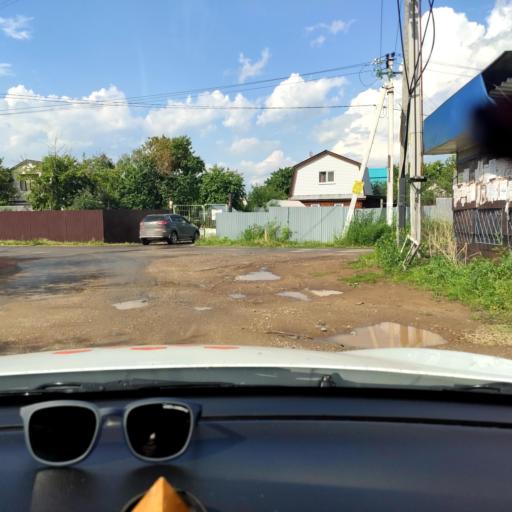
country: RU
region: Tatarstan
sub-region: Zelenodol'skiy Rayon
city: Vasil'yevo
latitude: 55.8255
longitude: 48.7257
